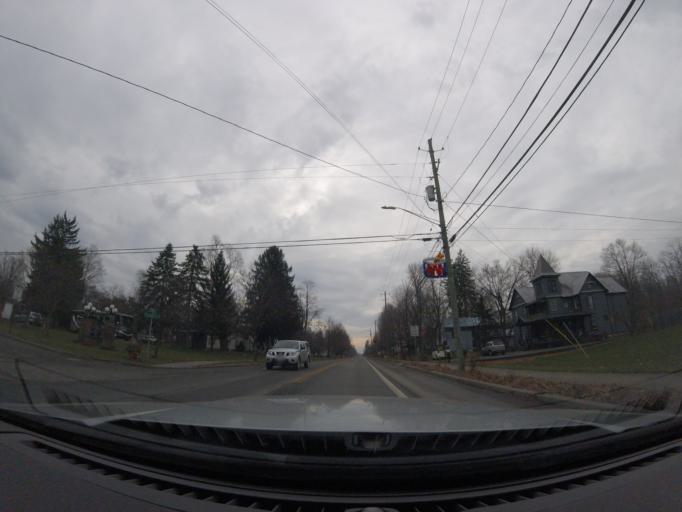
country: US
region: New York
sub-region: Schuyler County
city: Watkins Glen
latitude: 42.4174
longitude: -76.8495
